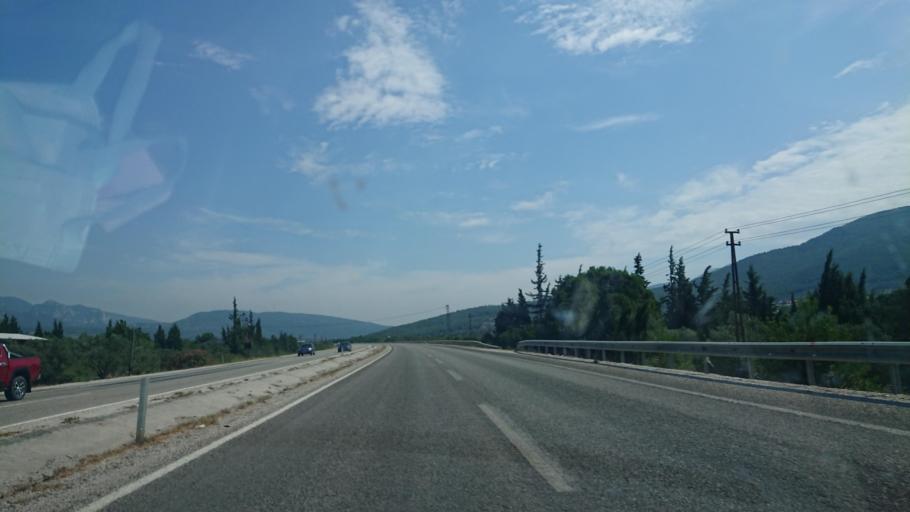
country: TR
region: Izmir
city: Dagkizilca
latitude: 38.2927
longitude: 27.4063
